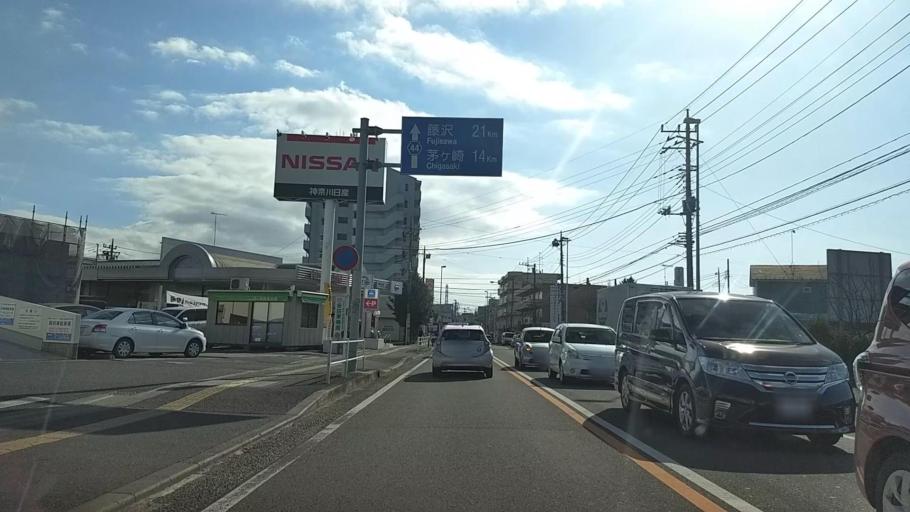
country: JP
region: Kanagawa
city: Isehara
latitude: 35.4023
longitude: 139.3133
